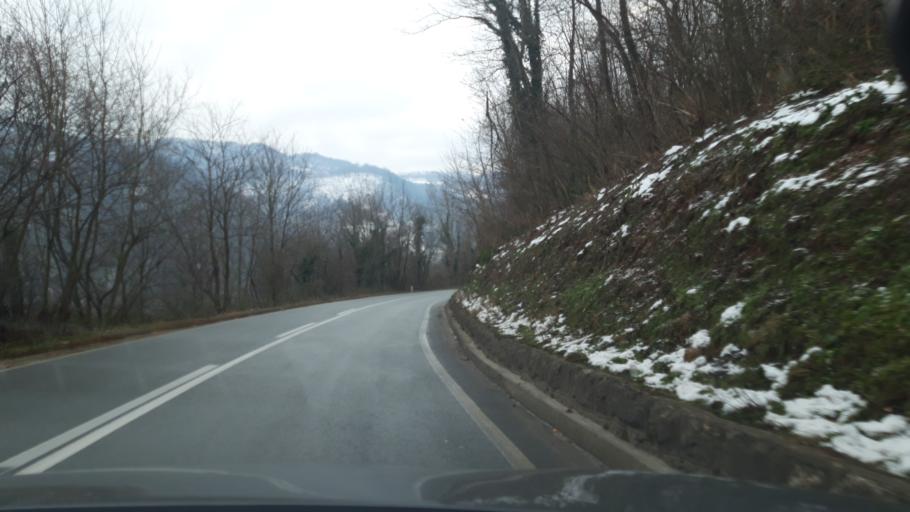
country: RS
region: Central Serbia
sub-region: Macvanski Okrug
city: Mali Zvornik
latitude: 44.3388
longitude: 19.1303
